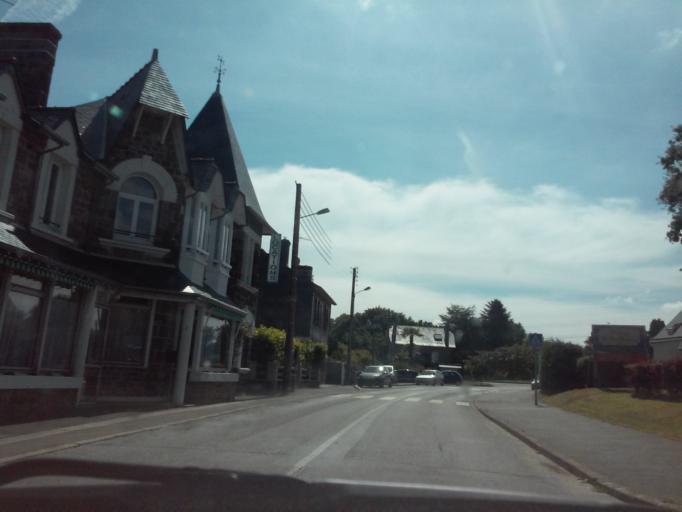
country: FR
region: Brittany
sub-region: Departement d'Ille-et-Vilaine
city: La Richardais
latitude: 48.6186
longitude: -2.0378
